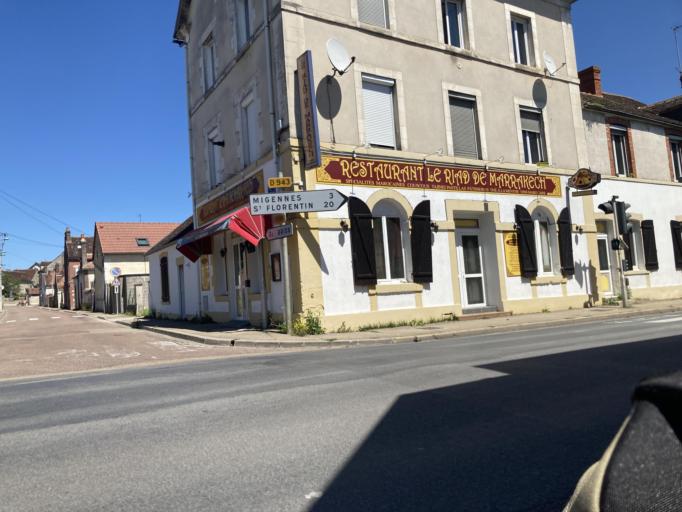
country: FR
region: Bourgogne
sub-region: Departement de l'Yonne
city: Laroche-Saint-Cydroine
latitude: 47.9640
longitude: 3.4846
